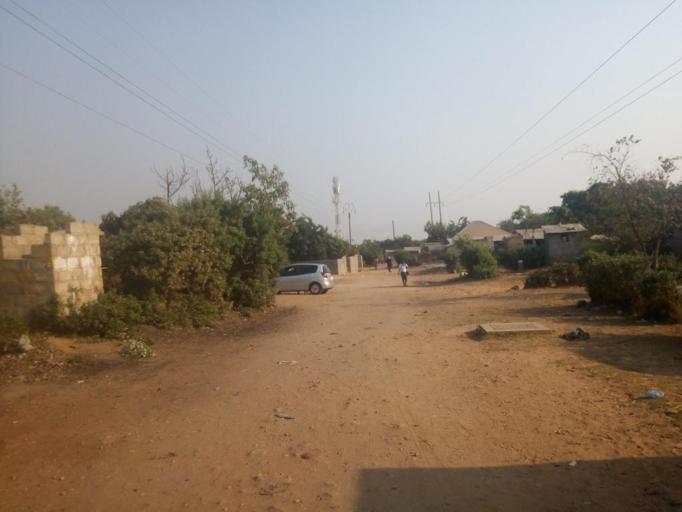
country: ZM
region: Lusaka
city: Lusaka
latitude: -15.4018
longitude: 28.3690
